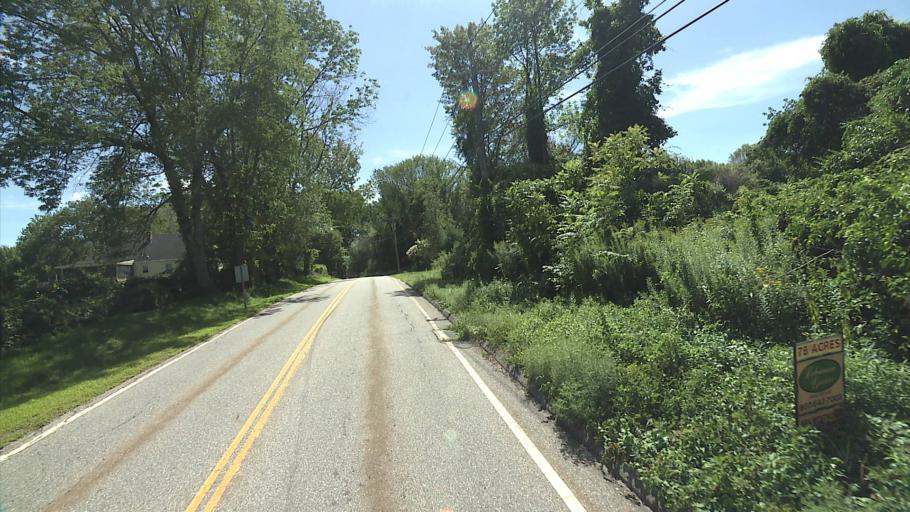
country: US
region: Connecticut
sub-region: Windham County
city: Windham
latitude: 41.7623
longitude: -72.0594
